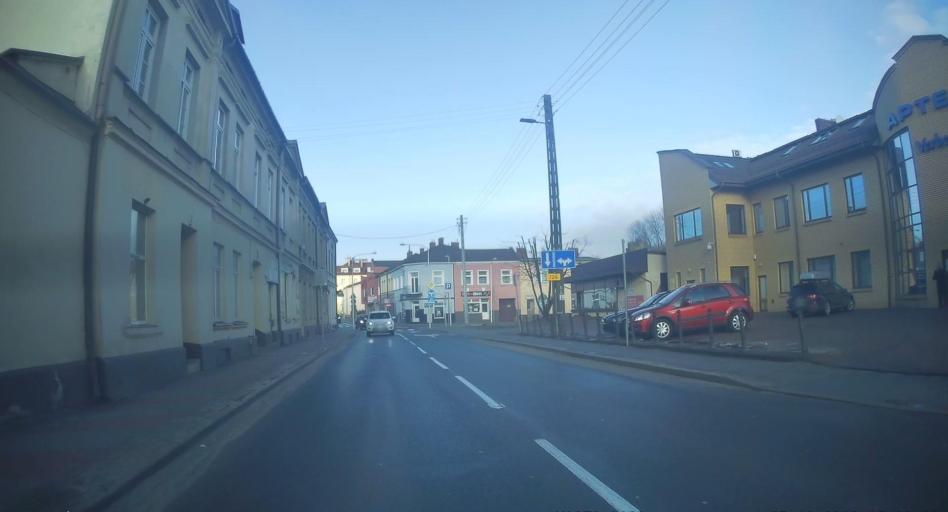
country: PL
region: Lodz Voivodeship
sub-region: Powiat rawski
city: Rawa Mazowiecka
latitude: 51.7640
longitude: 20.2548
